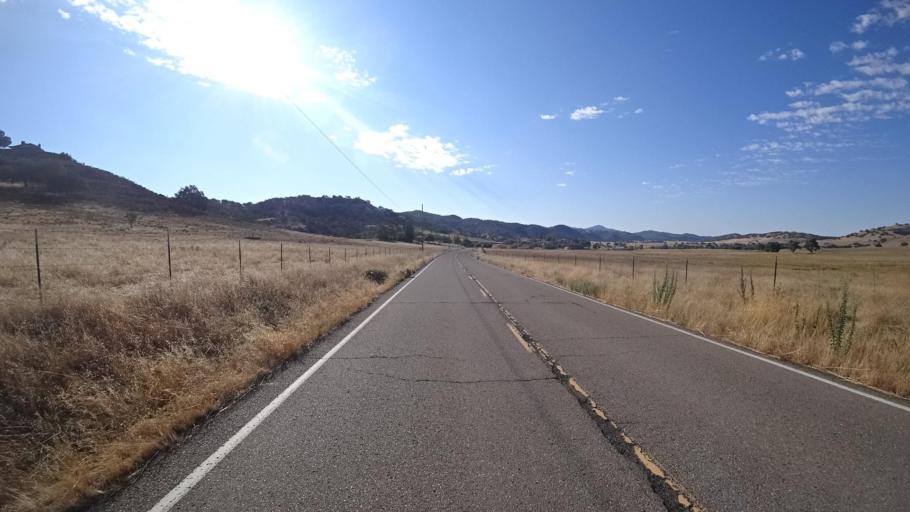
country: US
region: California
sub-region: San Diego County
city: Julian
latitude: 33.1397
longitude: -116.6841
